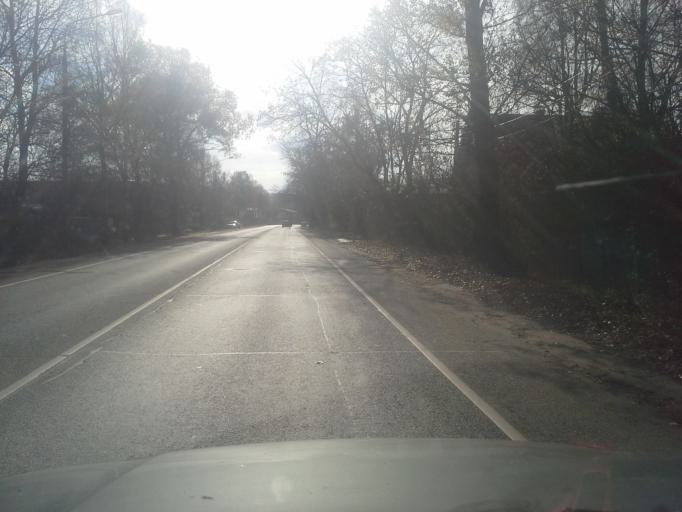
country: RU
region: Moskovskaya
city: Zvenigorod
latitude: 55.7189
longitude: 36.8653
